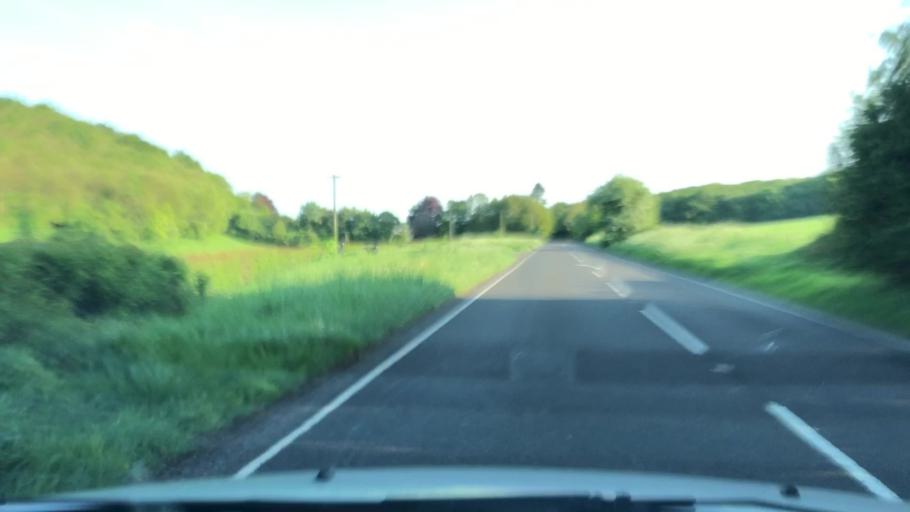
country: GB
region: England
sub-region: Hampshire
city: Alton
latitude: 51.1633
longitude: -0.9896
